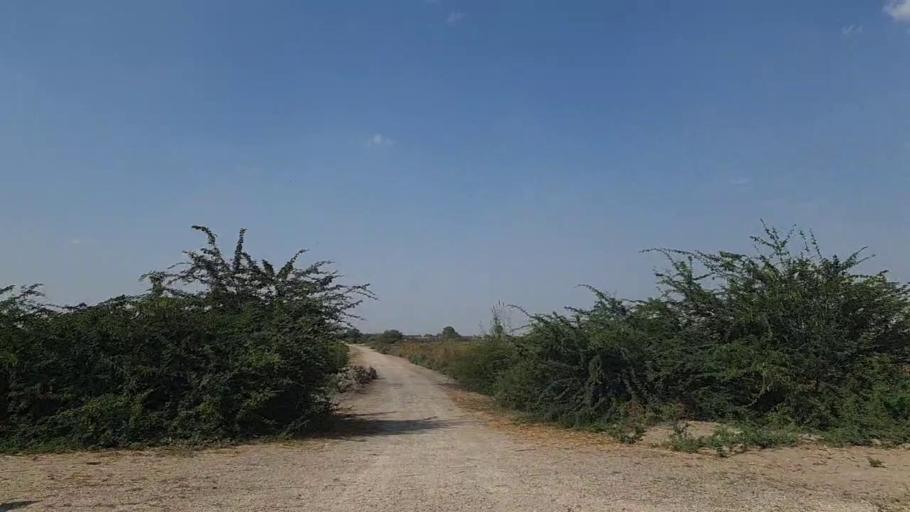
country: PK
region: Sindh
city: Jati
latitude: 24.5097
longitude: 68.2955
